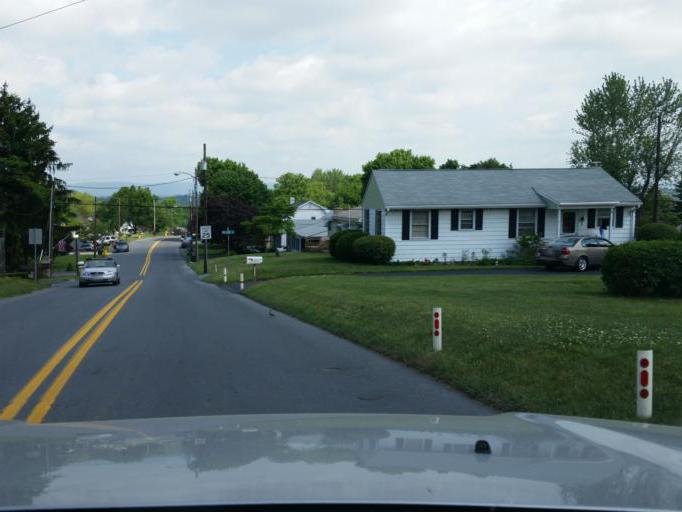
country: US
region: Pennsylvania
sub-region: Dauphin County
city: Bressler
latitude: 40.2421
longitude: -76.8154
